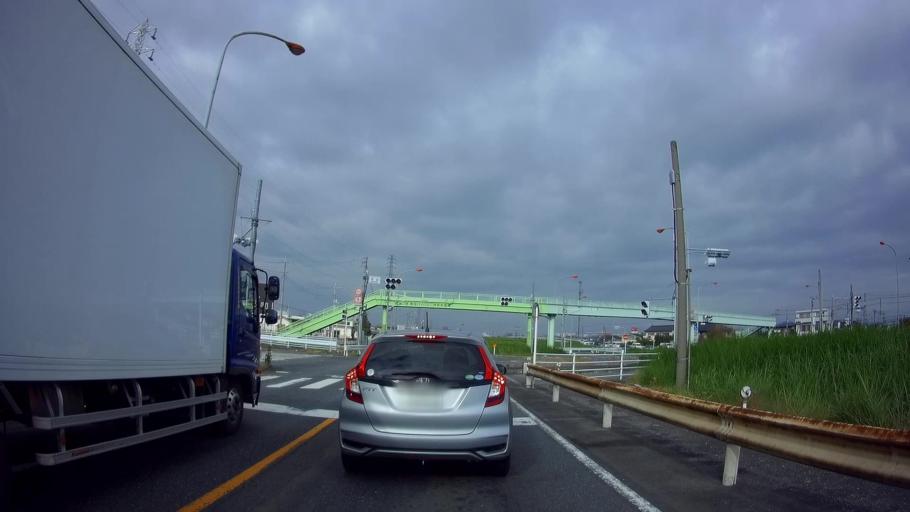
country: JP
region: Saitama
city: Gyoda
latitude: 36.1317
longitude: 139.4435
